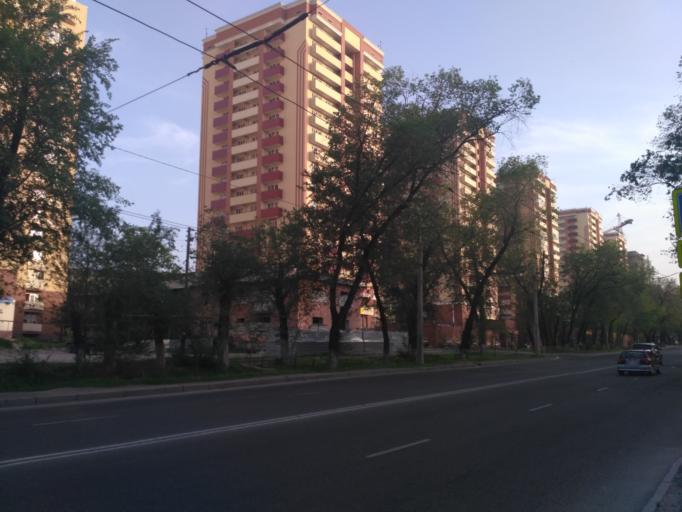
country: KZ
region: Almaty Qalasy
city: Almaty
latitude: 43.2155
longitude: 76.8738
